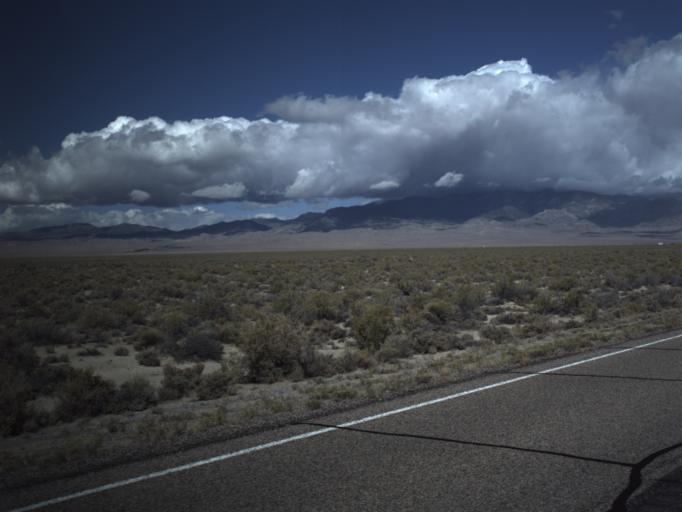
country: US
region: Nevada
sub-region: White Pine County
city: McGill
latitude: 39.0199
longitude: -114.0354
